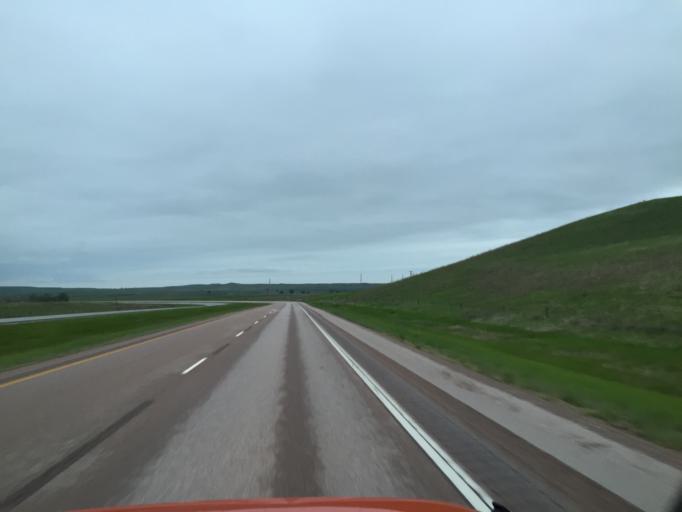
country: US
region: South Dakota
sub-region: Pennington County
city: Colonial Pine Hills
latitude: 43.7103
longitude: -103.2226
